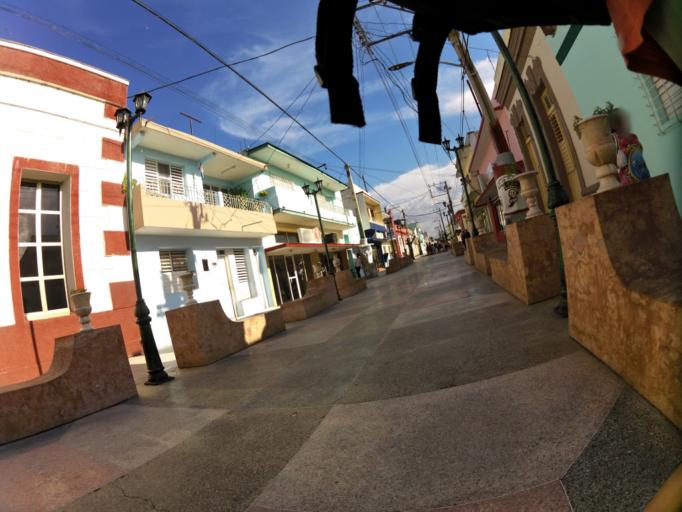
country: CU
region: Granma
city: Bayamo
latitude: 20.3701
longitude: -76.6469
